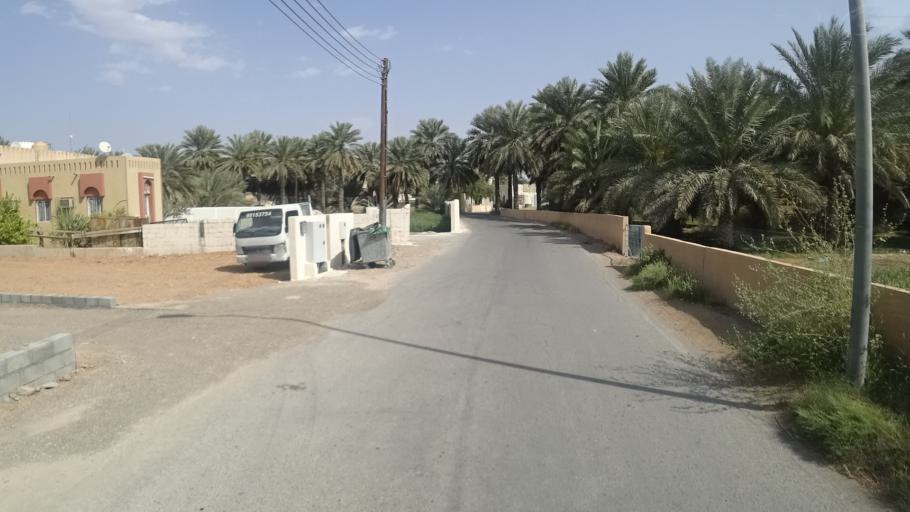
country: OM
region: Muhafazat ad Dakhiliyah
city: Bahla'
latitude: 23.0981
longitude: 57.3055
